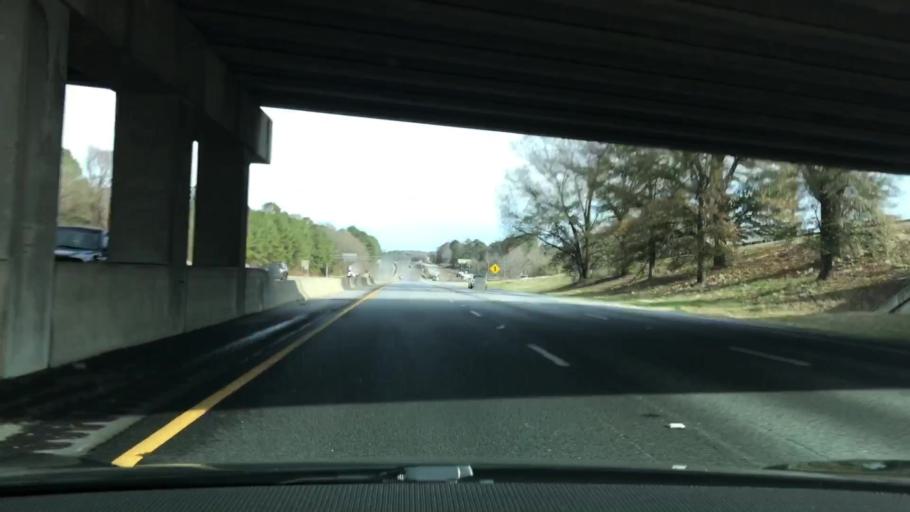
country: US
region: Georgia
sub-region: Newton County
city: Porterdale
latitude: 33.6158
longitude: -83.9205
